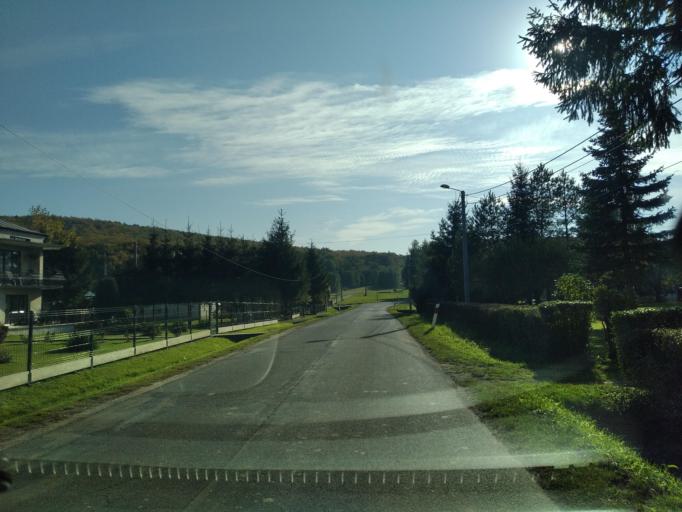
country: PL
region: Subcarpathian Voivodeship
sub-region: Powiat sanocki
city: Besko
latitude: 49.5742
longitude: 21.9463
